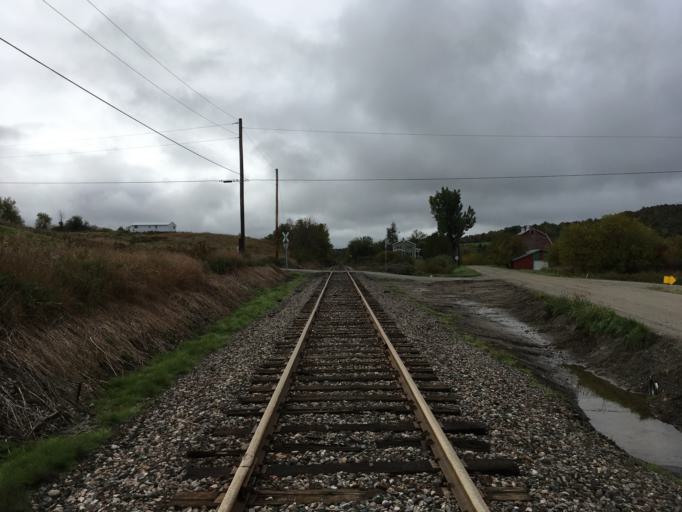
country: US
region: Vermont
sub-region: Orleans County
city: Newport
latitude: 44.8430
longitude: -72.2068
